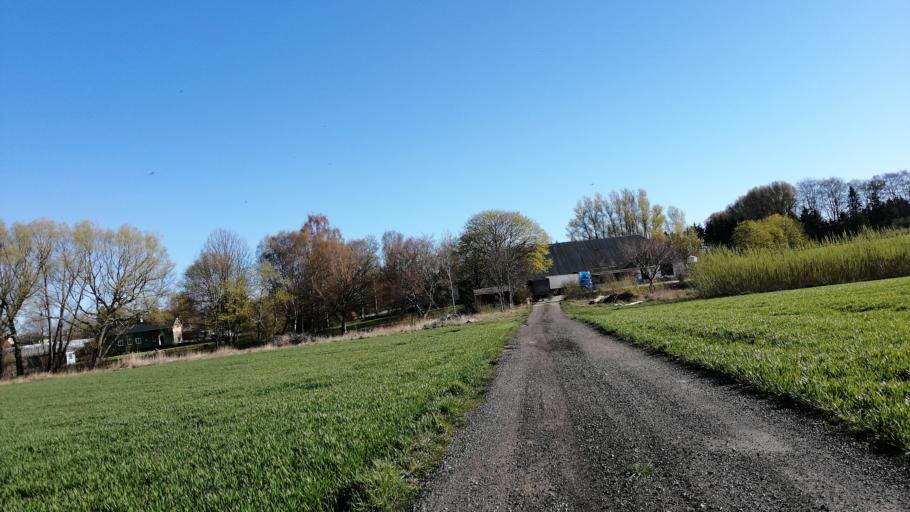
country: SE
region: Skane
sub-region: Landskrona
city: Asmundtorp
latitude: 55.8775
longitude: 13.0040
